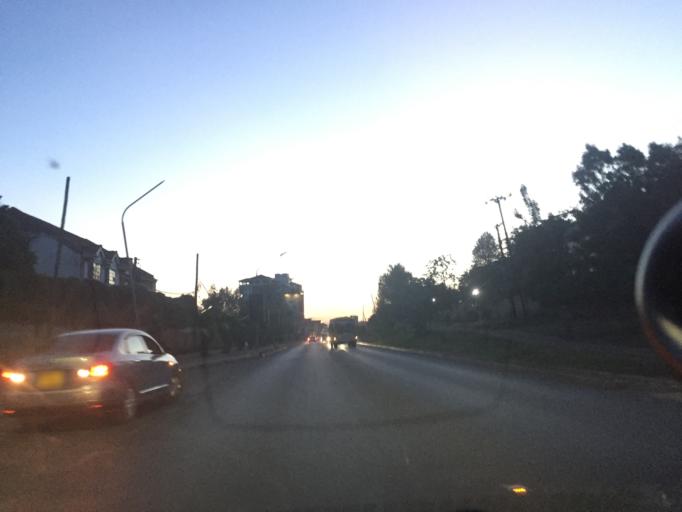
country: KE
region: Nairobi Area
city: Nairobi
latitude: -1.2800
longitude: 36.7899
